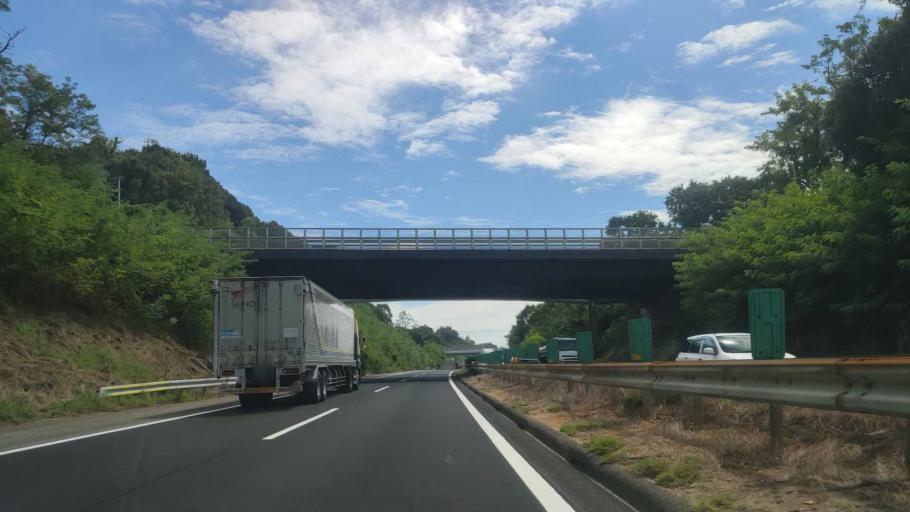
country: JP
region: Aichi
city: Okazaki
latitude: 34.9578
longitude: 137.1936
